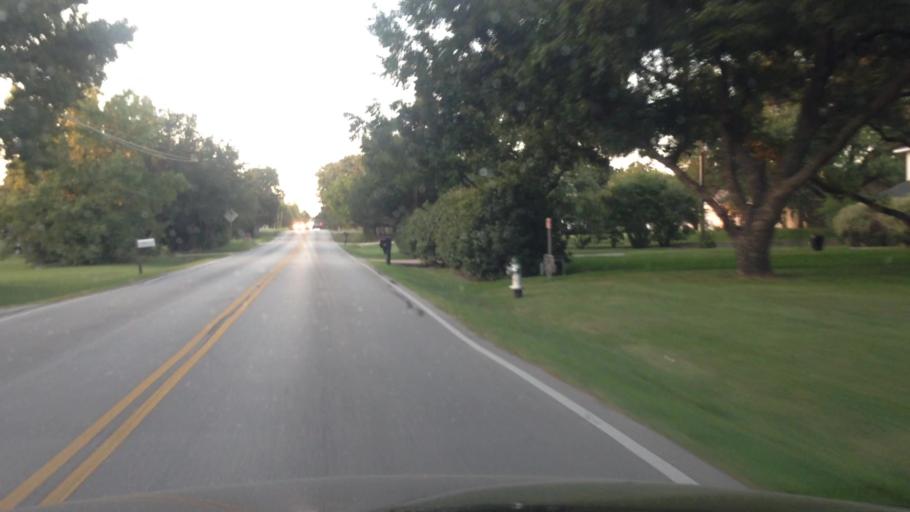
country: US
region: Texas
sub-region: Tarrant County
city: Keller
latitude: 32.9420
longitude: -97.2031
